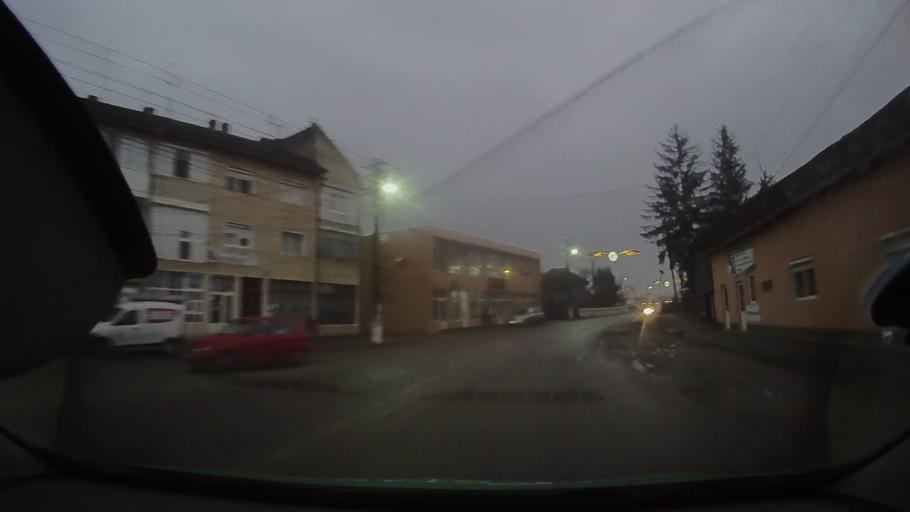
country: RO
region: Arad
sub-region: Comuna Beliu
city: Beliu
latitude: 46.4932
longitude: 21.9848
